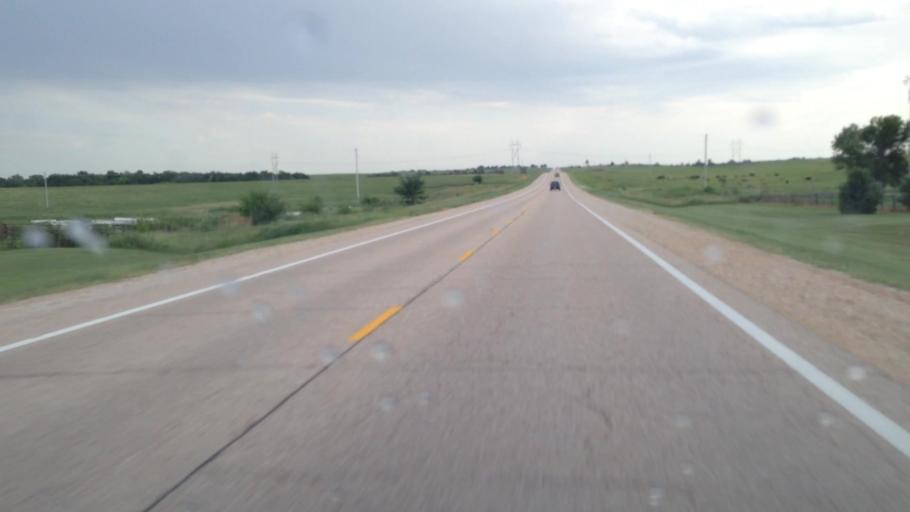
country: US
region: Kansas
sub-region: Coffey County
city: Burlington
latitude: 38.1643
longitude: -95.7390
